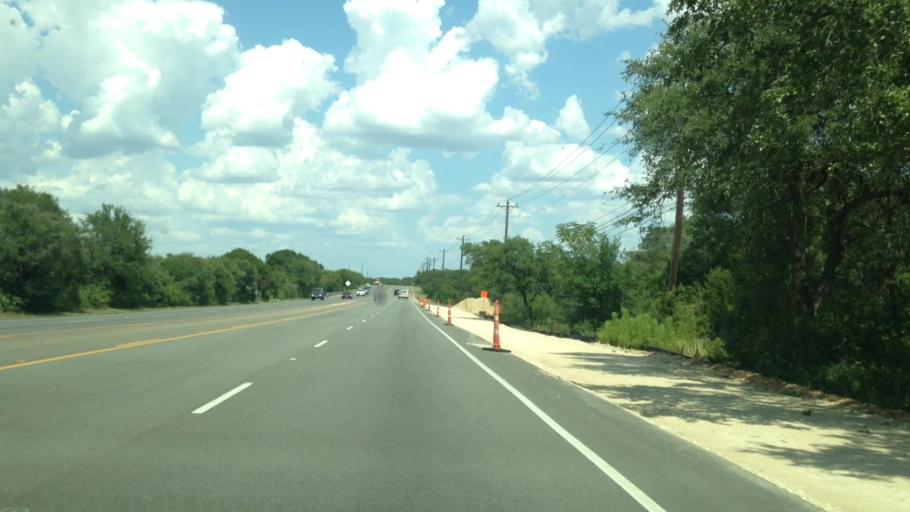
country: US
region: Texas
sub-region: Williamson County
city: Georgetown
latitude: 30.6324
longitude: -97.7367
